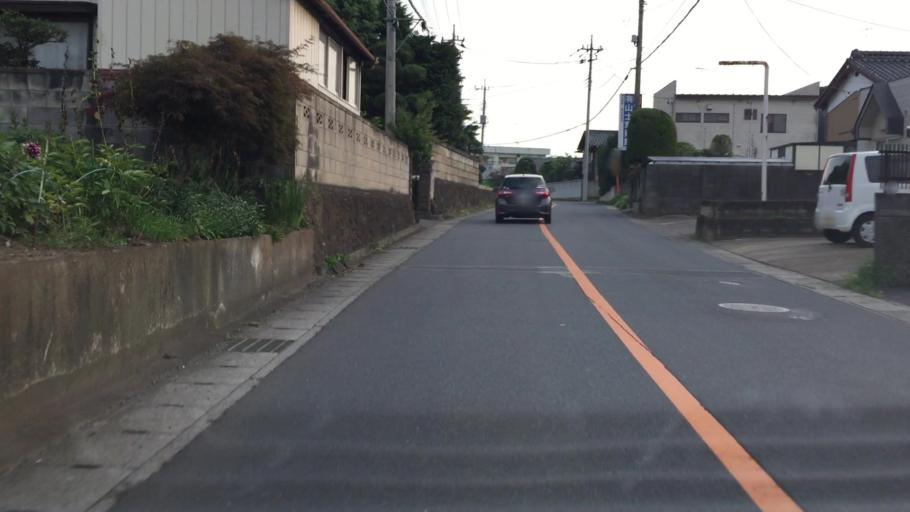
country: JP
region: Tochigi
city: Fujioka
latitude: 36.2724
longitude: 139.6535
